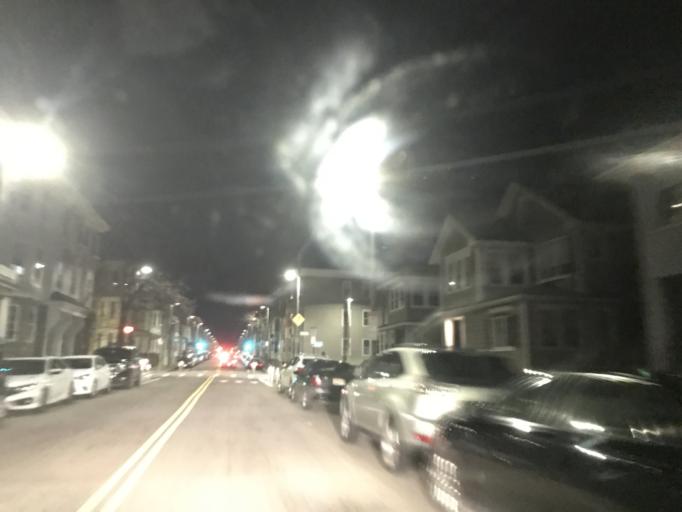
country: US
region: Massachusetts
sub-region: Suffolk County
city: South Boston
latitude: 42.3302
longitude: -71.0352
